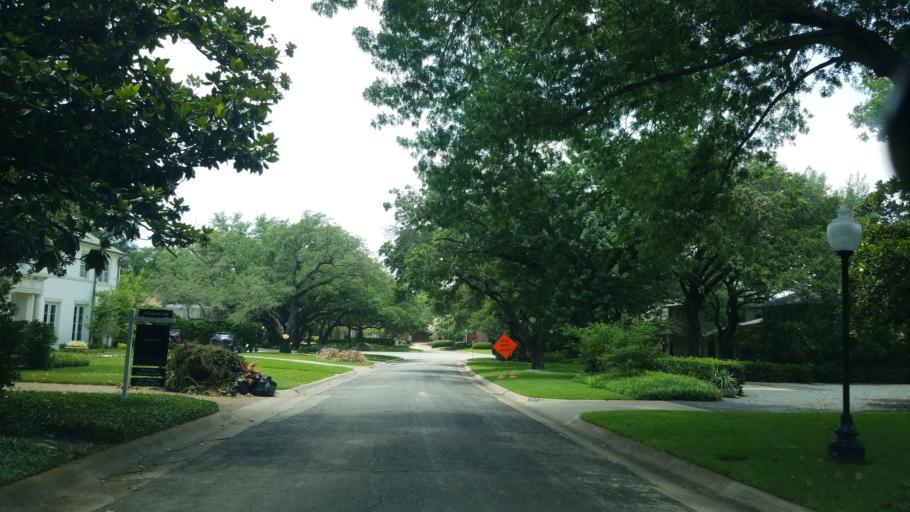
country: US
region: Texas
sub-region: Dallas County
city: University Park
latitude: 32.8438
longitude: -96.8203
